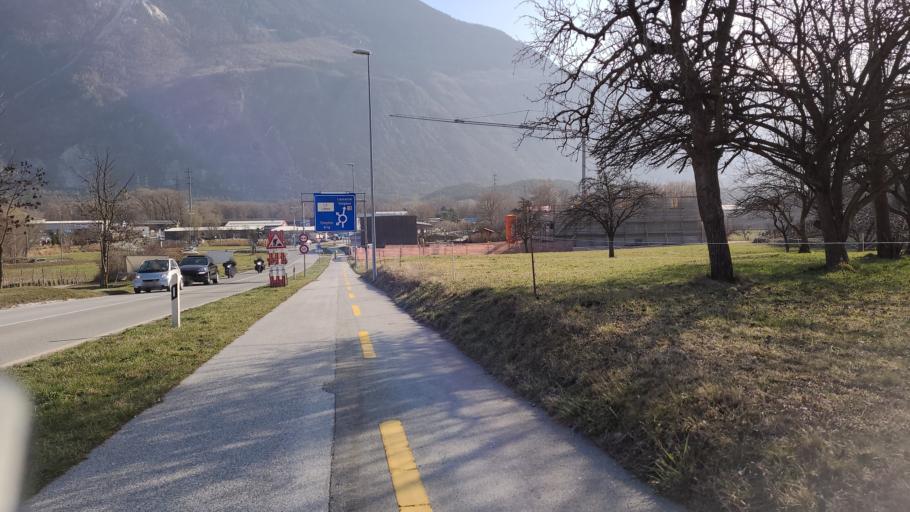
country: CH
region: Valais
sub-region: Leuk District
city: Salgesch
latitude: 46.3067
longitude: 7.5665
